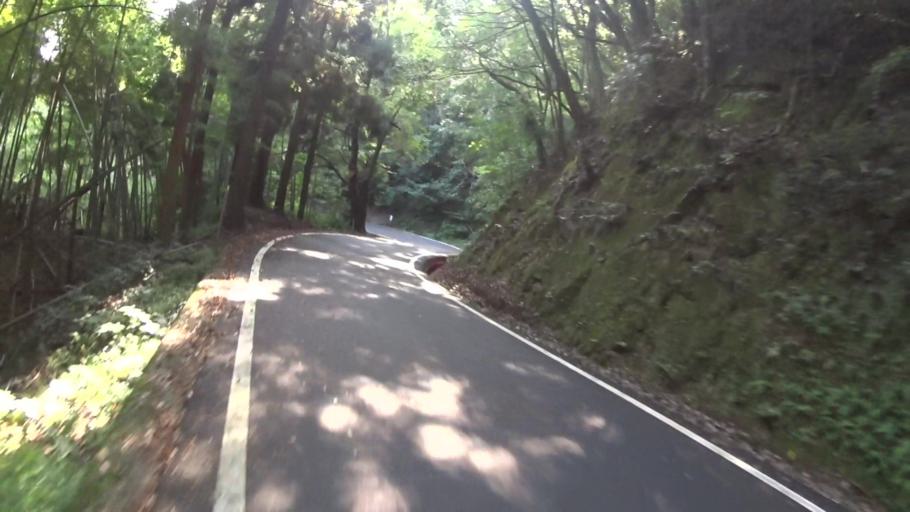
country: JP
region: Kyoto
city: Miyazu
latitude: 35.5648
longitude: 135.1432
